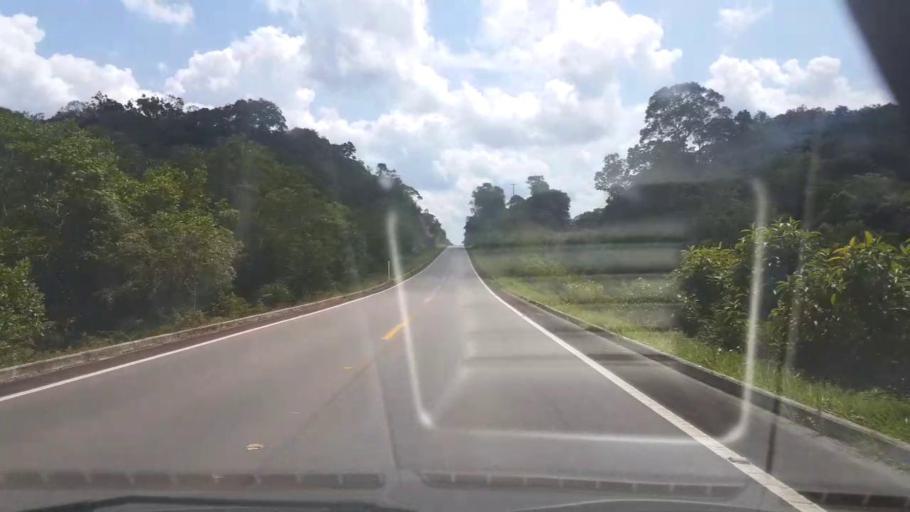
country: BR
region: Amazonas
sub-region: Rio Preto Da Eva
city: Rio Preto da Eva
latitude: -2.4930
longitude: -60.0342
